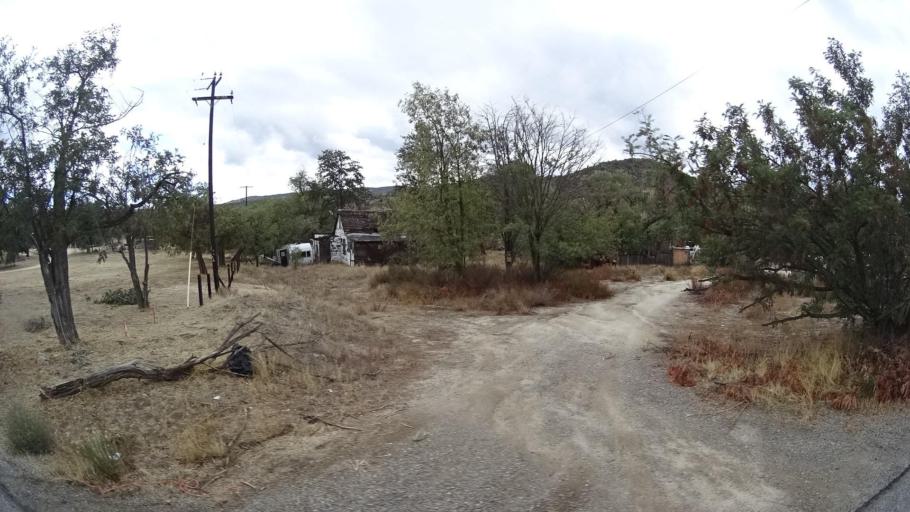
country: US
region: California
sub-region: San Diego County
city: Campo
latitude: 32.6380
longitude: -116.4322
